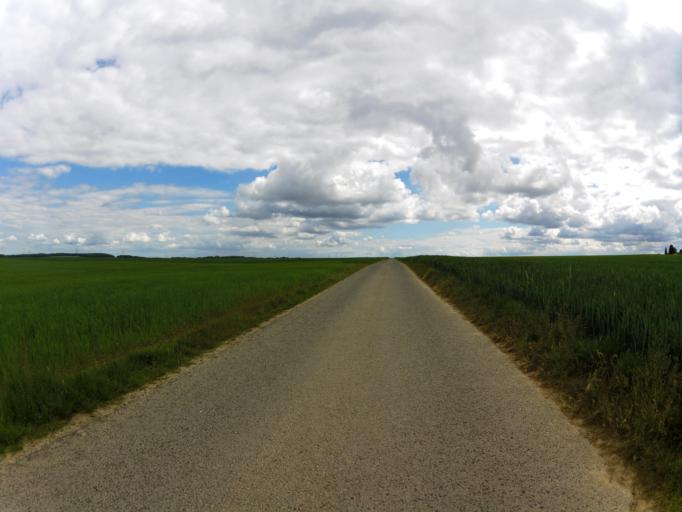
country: DE
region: Bavaria
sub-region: Regierungsbezirk Unterfranken
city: Gaukonigshofen
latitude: 49.6524
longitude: 10.0046
